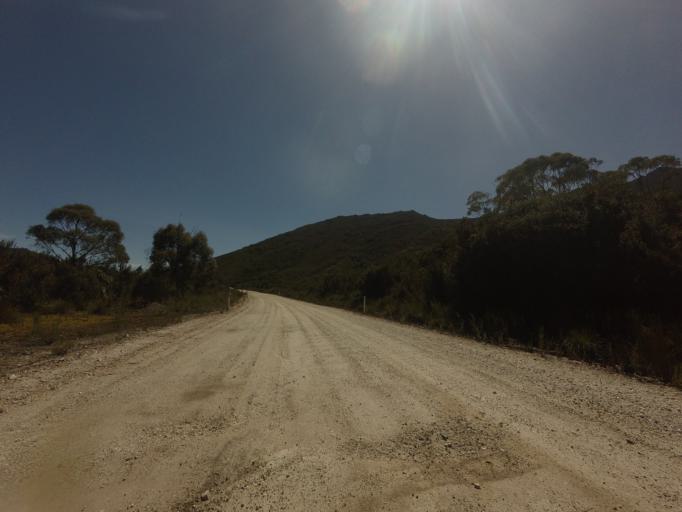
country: AU
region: Tasmania
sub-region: Huon Valley
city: Geeveston
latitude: -42.9384
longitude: 146.3482
